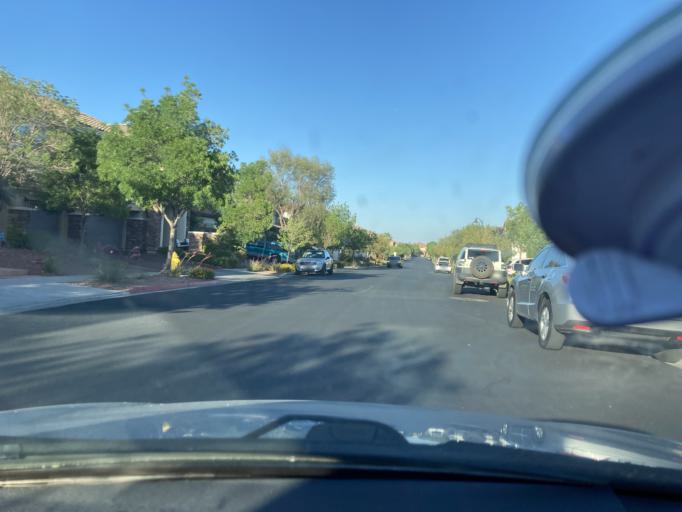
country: US
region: Nevada
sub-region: Clark County
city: Summerlin South
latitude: 36.1577
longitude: -115.3507
